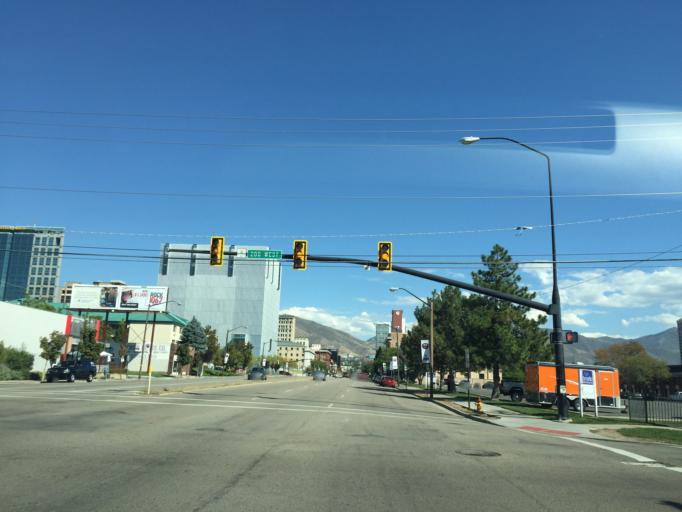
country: US
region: Utah
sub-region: Salt Lake County
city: Salt Lake City
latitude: 40.7605
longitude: -111.8969
